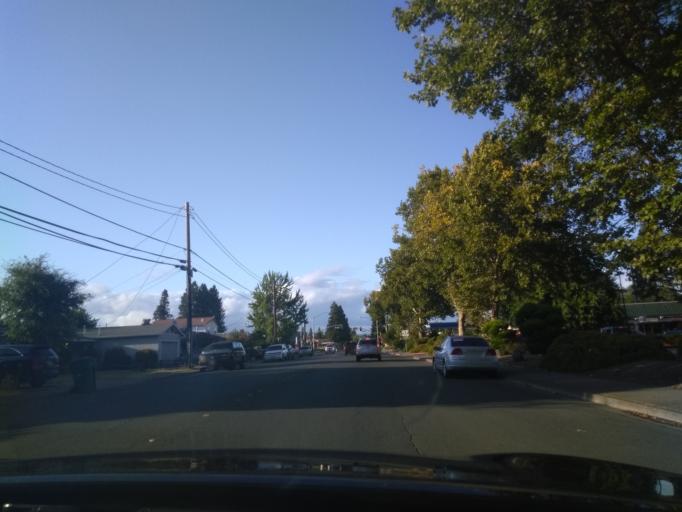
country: US
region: California
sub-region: Mendocino County
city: Ukiah
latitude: 39.1501
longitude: -123.1990
